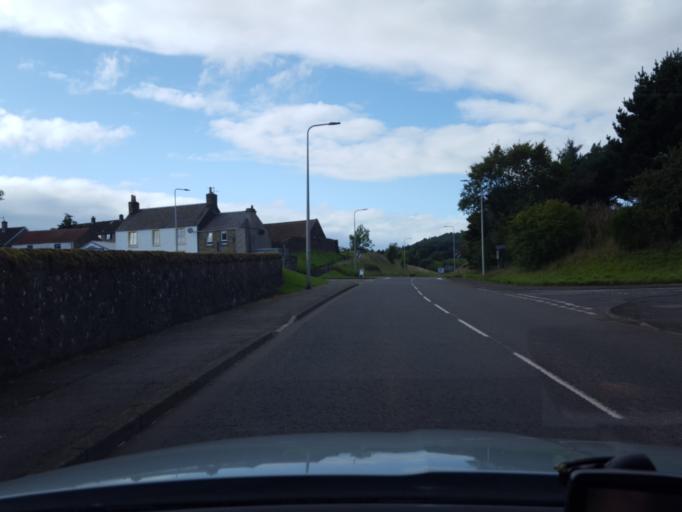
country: GB
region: Scotland
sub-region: Fife
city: Auchtermuchty
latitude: 56.2785
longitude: -3.2658
